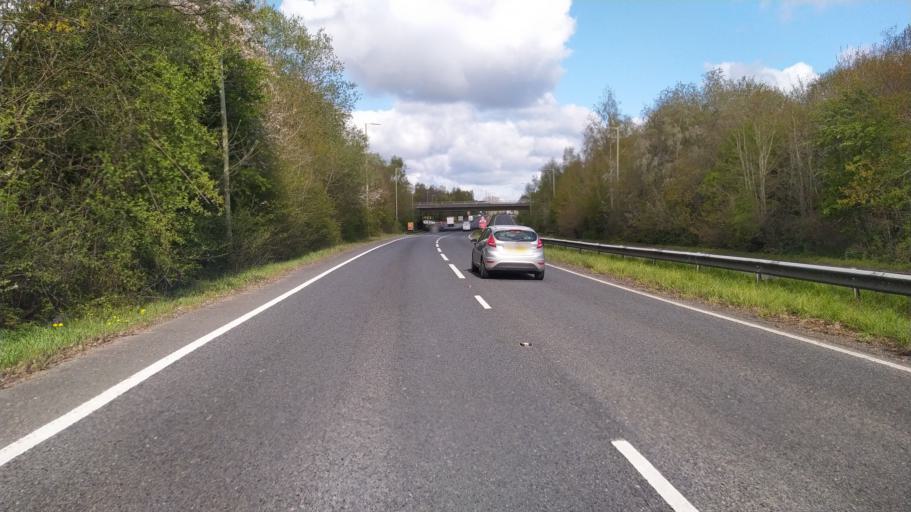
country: GB
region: England
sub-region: Hampshire
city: Totton
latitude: 50.9027
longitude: -1.4987
